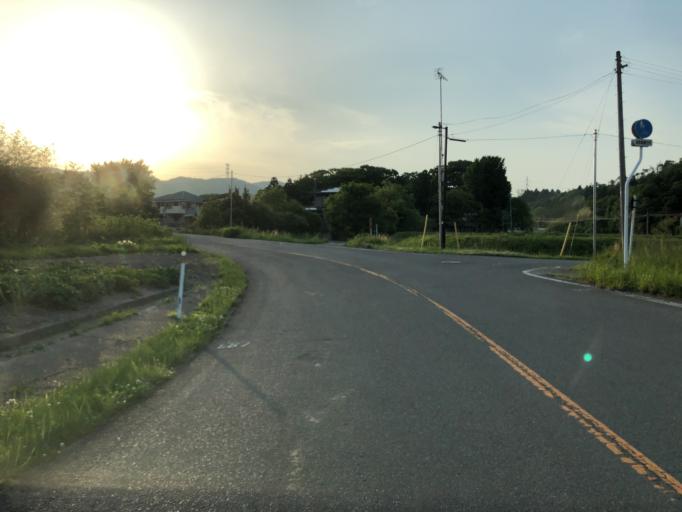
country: JP
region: Fukushima
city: Iwaki
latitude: 37.2175
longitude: 140.9750
